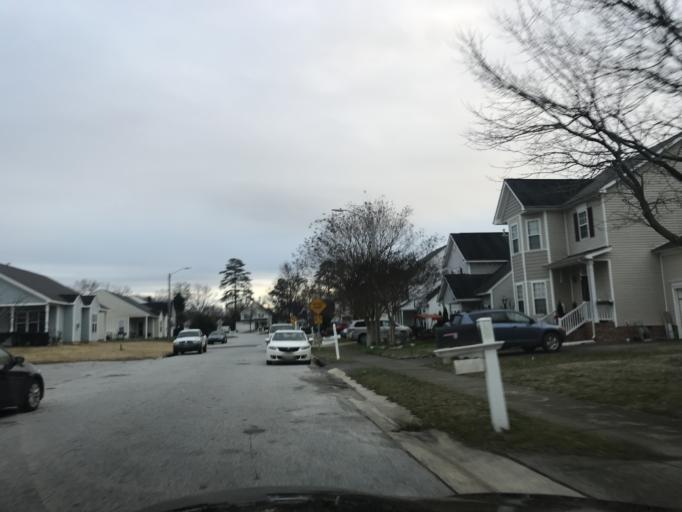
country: US
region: North Carolina
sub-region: Wake County
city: Garner
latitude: 35.7493
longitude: -78.6027
